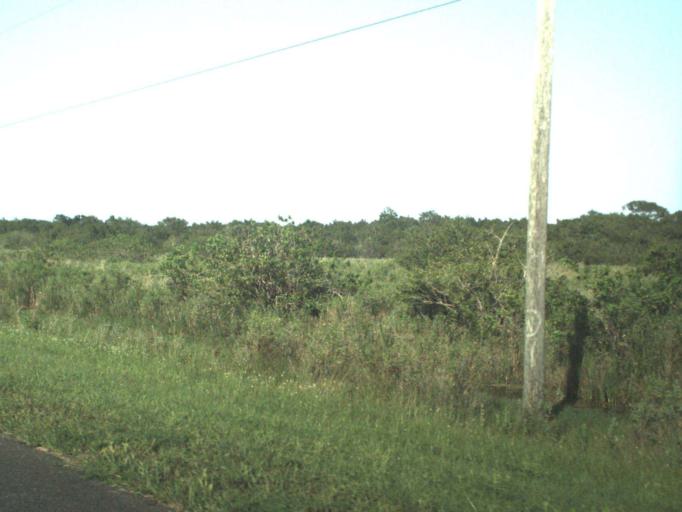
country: US
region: Florida
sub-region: Volusia County
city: Oak Hill
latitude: 28.8189
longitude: -80.8615
